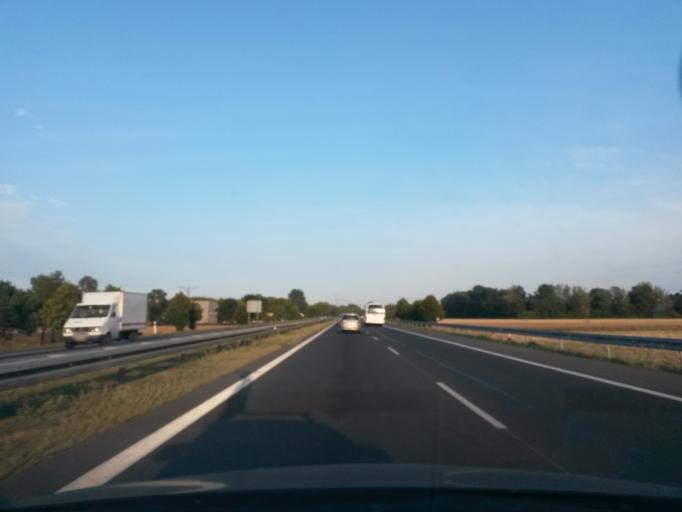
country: PL
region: Masovian Voivodeship
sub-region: Powiat nowodworski
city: Nowy Dwor Mazowiecki
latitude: 52.4157
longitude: 20.6844
